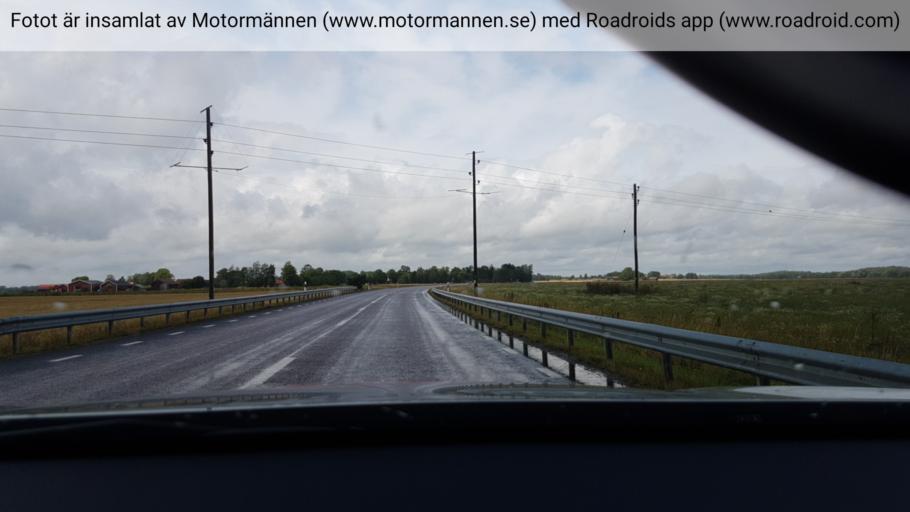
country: SE
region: Uppsala
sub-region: Osthammars Kommun
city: Bjorklinge
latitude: 59.9187
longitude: 17.5079
